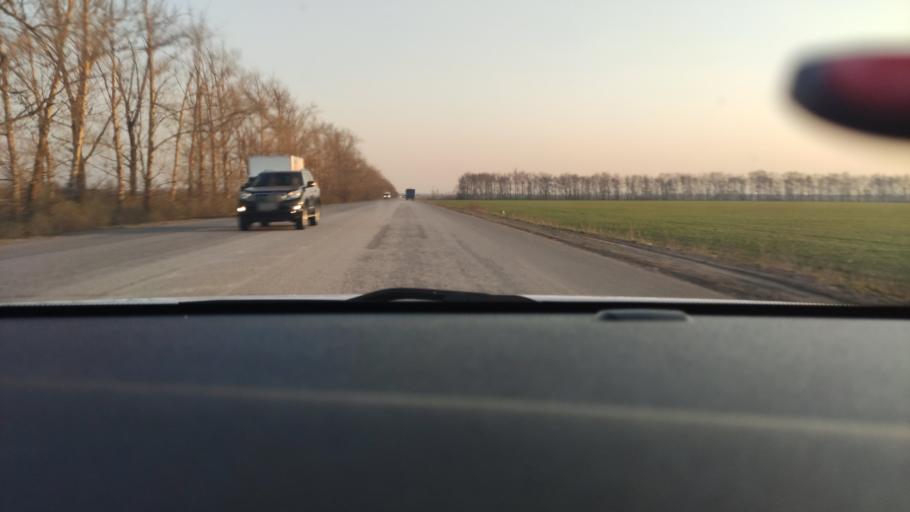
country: RU
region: Voronezj
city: Maslovka
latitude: 51.4417
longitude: 39.3024
